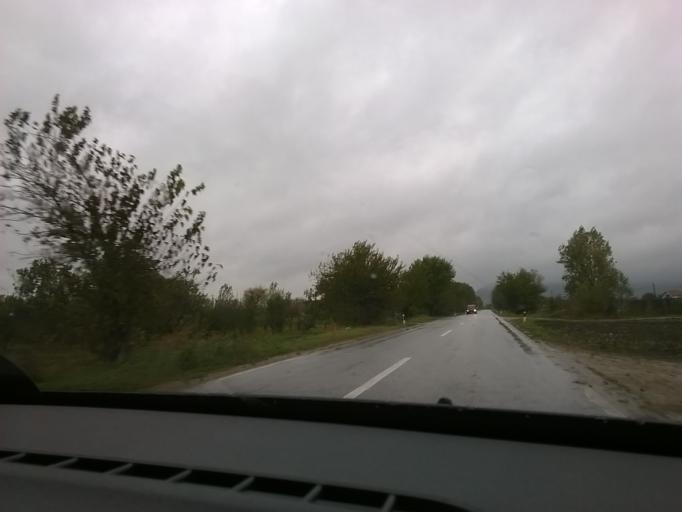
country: RS
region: Autonomna Pokrajina Vojvodina
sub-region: Juznobanatski Okrug
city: Vrsac
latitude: 45.0868
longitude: 21.2962
